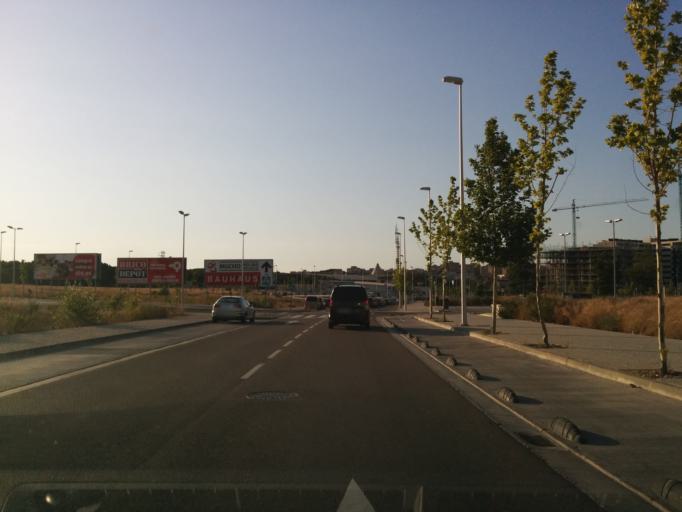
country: ES
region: Aragon
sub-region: Provincia de Zaragoza
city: Zaragoza
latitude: 41.6162
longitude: -0.8753
